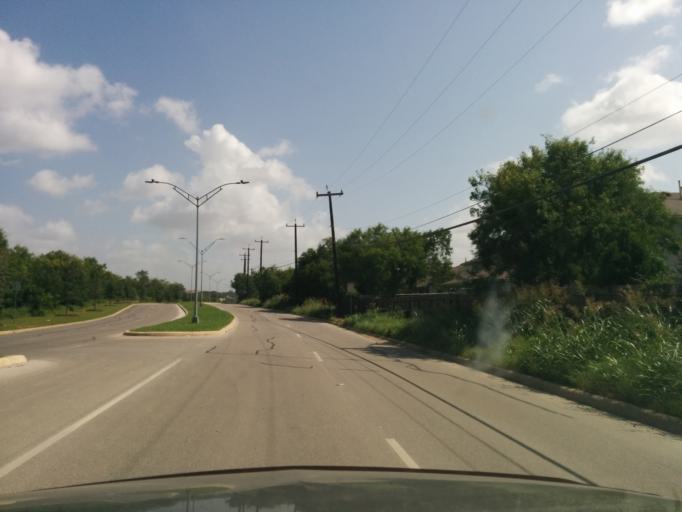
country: US
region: Texas
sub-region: Bexar County
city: Shavano Park
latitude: 29.5685
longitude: -98.6177
